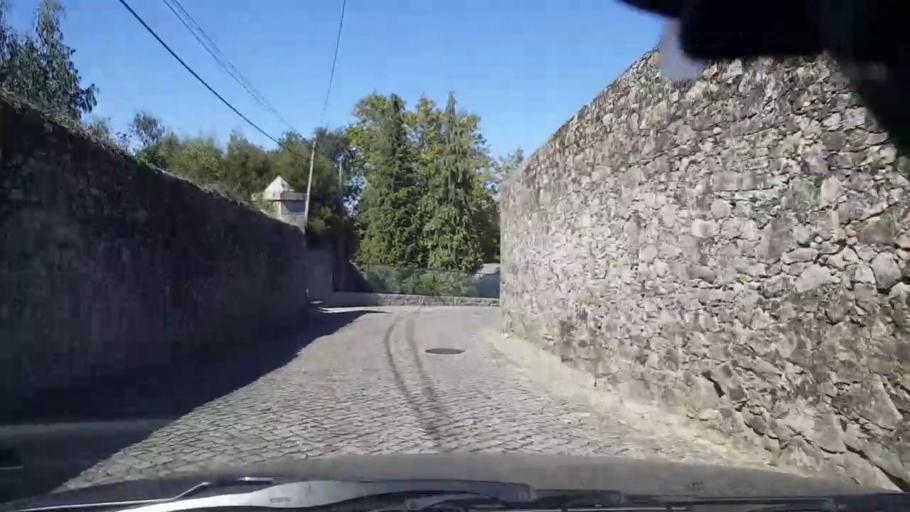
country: PT
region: Porto
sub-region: Vila do Conde
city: Arvore
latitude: 41.3302
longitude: -8.6719
